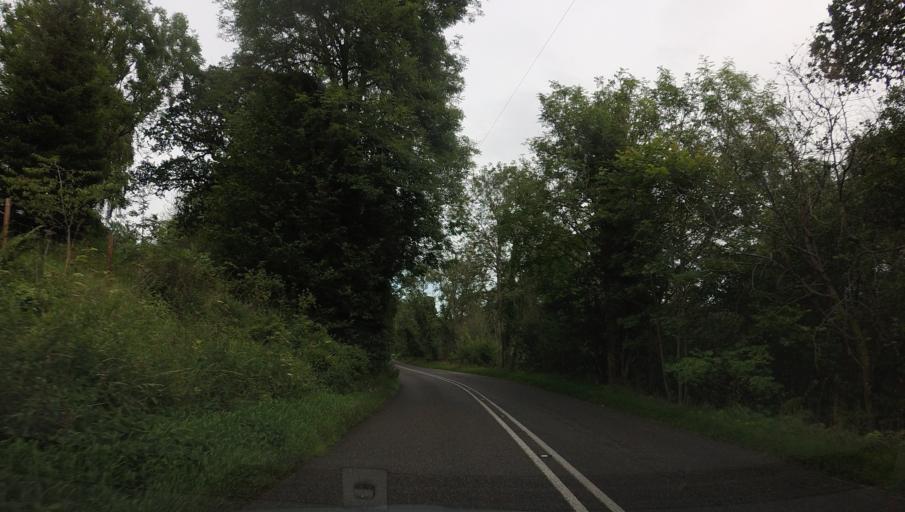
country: GB
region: Scotland
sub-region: Aberdeenshire
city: Torphins
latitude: 57.0630
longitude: -2.5675
